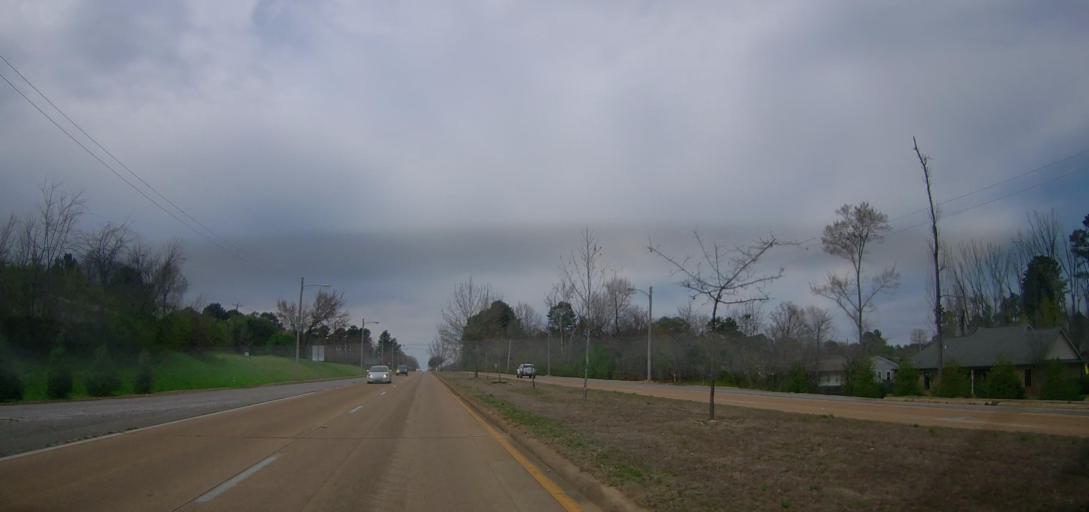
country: US
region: Mississippi
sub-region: Lee County
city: Tupelo
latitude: 34.2788
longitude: -88.7263
